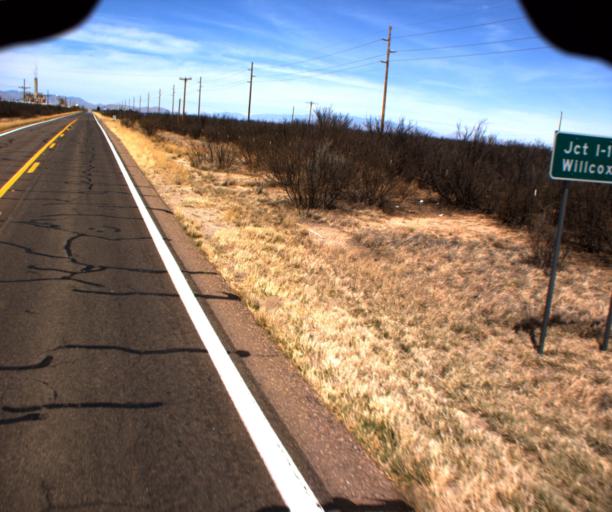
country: US
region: Arizona
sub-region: Cochise County
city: Willcox
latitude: 32.0384
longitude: -109.8802
